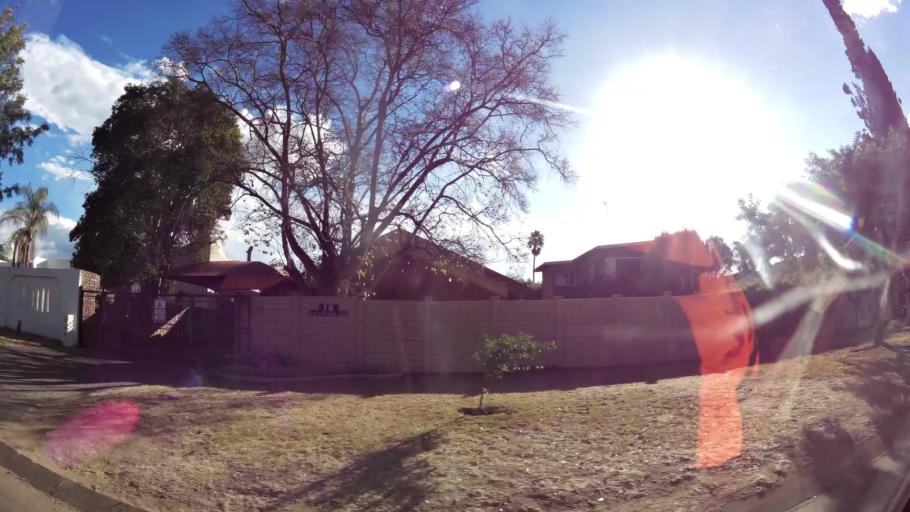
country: ZA
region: Limpopo
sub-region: Capricorn District Municipality
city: Polokwane
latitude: -23.9294
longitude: 29.4525
